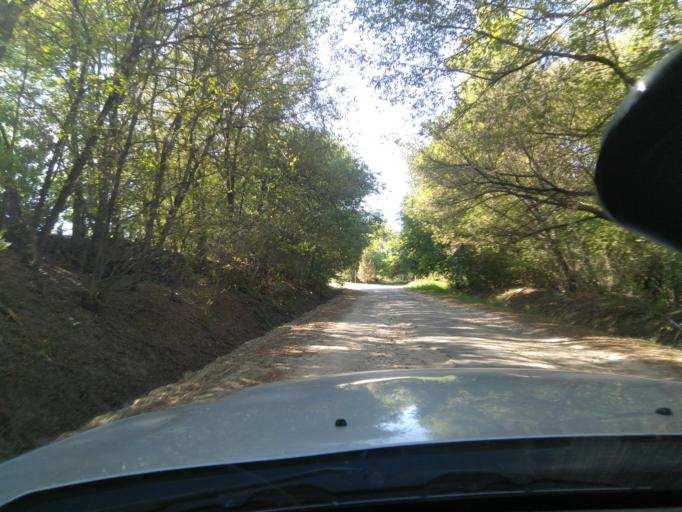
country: HU
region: Fejer
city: Baracska
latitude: 47.3160
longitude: 18.7164
